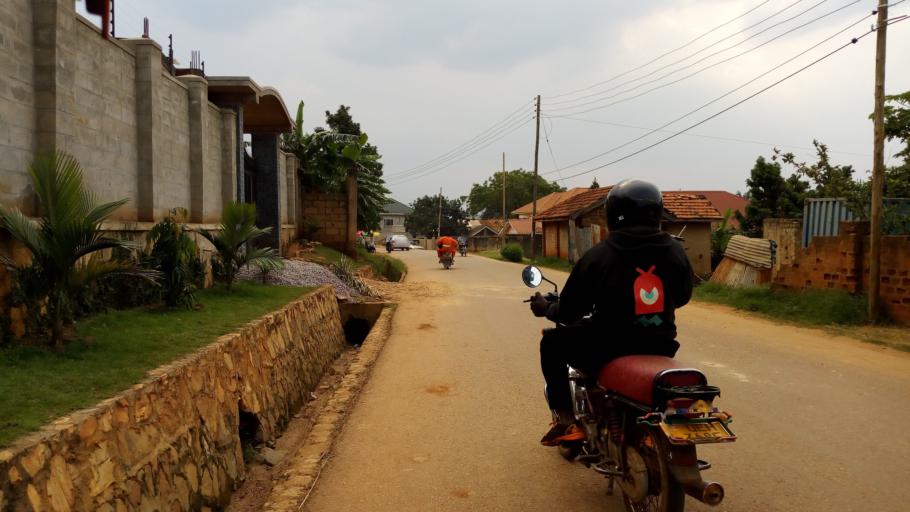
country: UG
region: Central Region
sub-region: Wakiso District
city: Kireka
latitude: 0.3172
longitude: 32.6457
